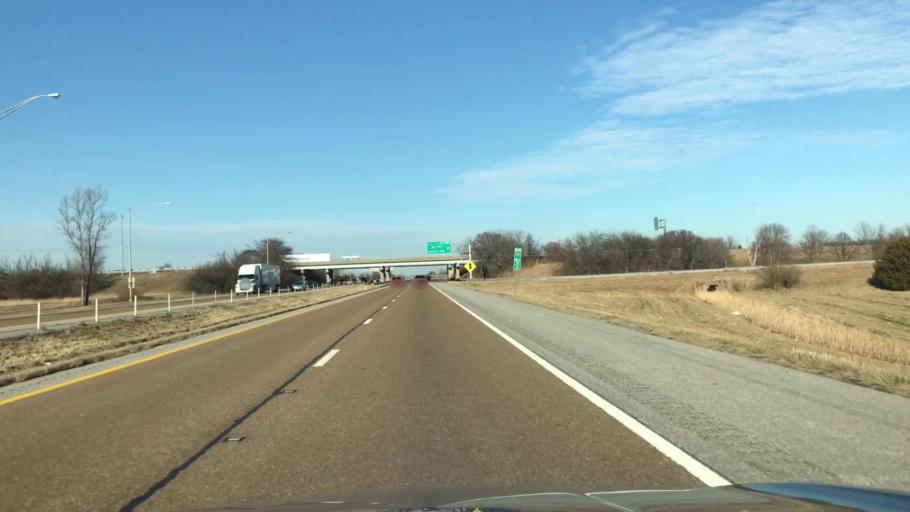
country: US
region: Illinois
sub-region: Madison County
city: Troy
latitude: 38.7500
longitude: -89.9077
